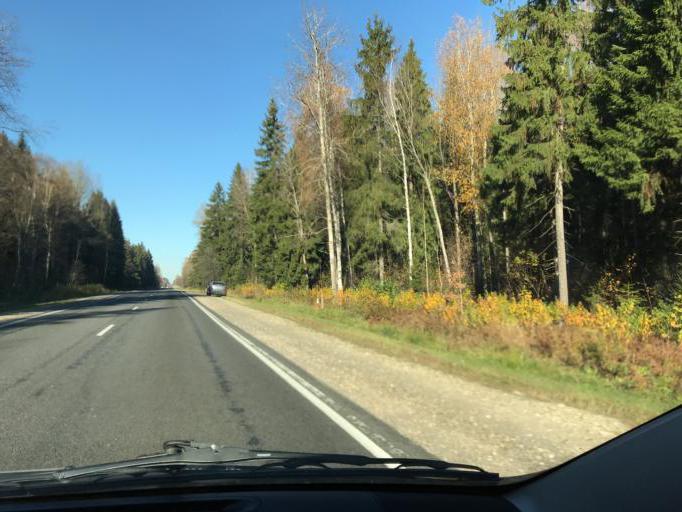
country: BY
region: Vitebsk
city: Polatsk
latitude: 55.5233
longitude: 28.7301
